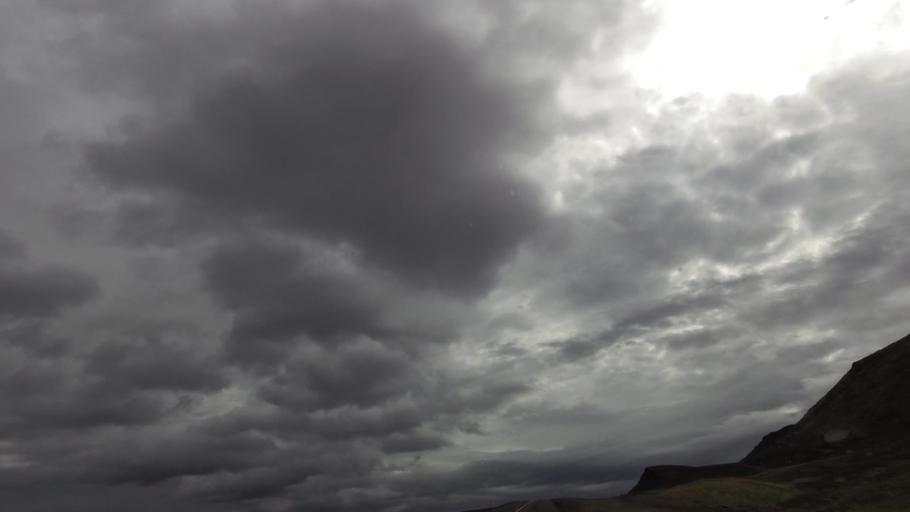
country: IS
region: West
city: Stykkisholmur
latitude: 65.5075
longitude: -22.1125
